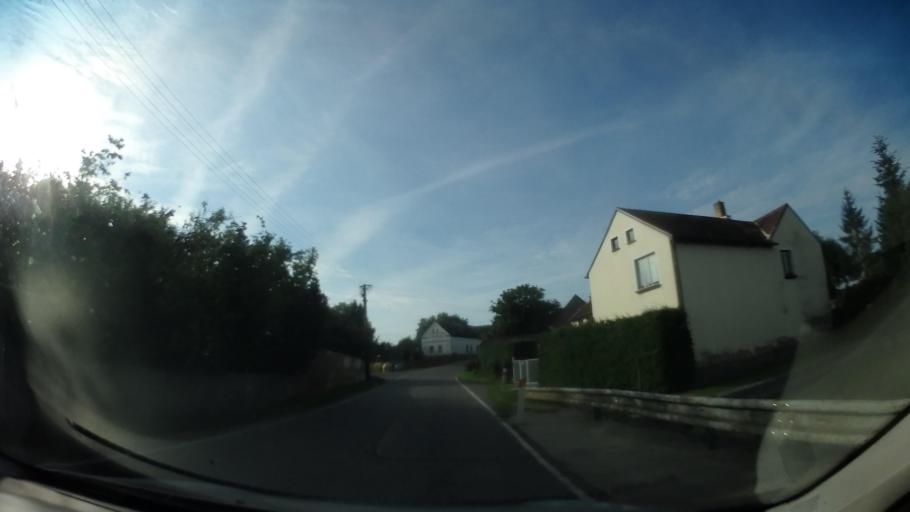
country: CZ
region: Jihocesky
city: Cimelice
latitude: 49.4746
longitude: 14.1519
